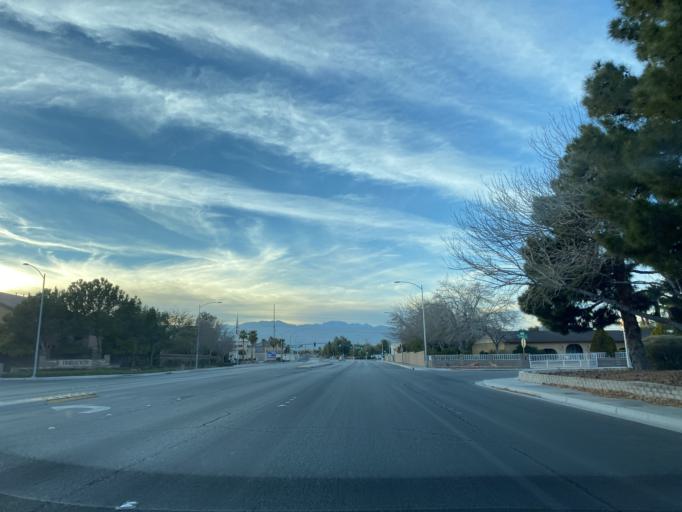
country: US
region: Nevada
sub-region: Clark County
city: Las Vegas
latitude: 36.2630
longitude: -115.2399
